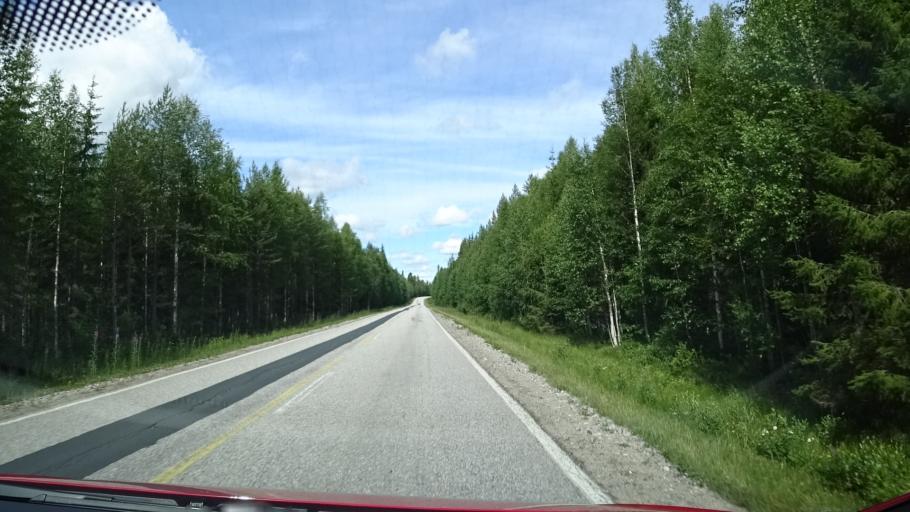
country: FI
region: Kainuu
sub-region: Kehys-Kainuu
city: Kuhmo
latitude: 64.4513
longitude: 29.7808
